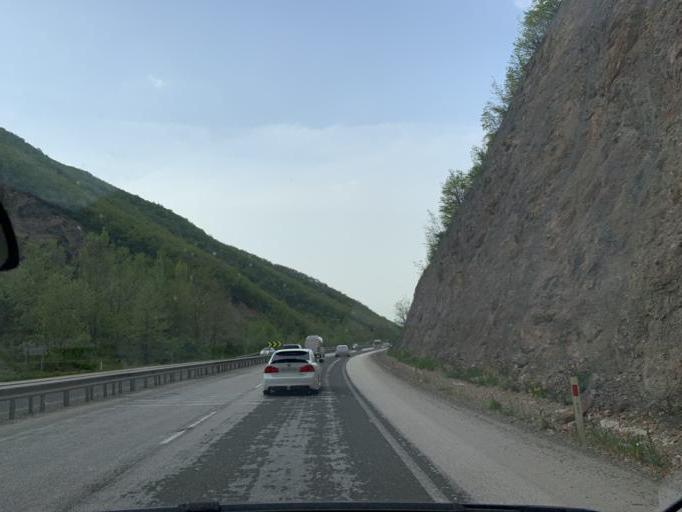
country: TR
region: Bursa
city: Kursunlu
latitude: 40.0009
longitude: 29.6525
